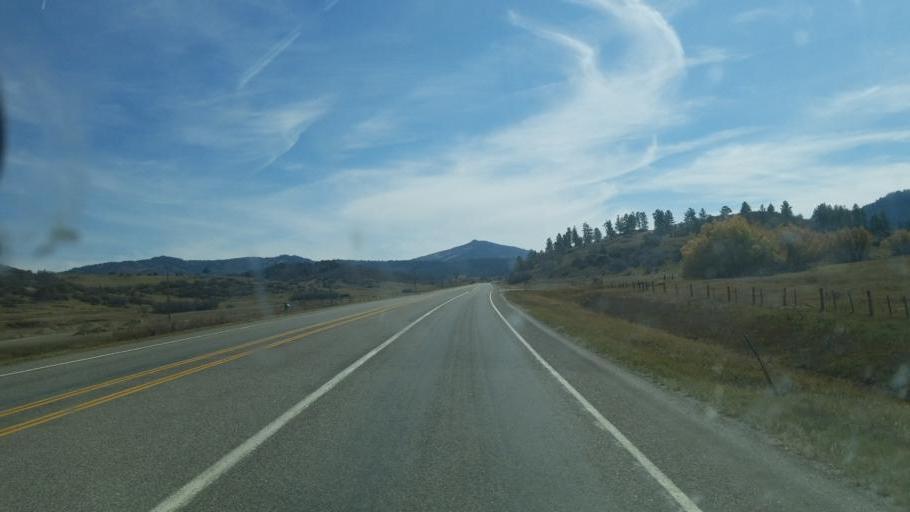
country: US
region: New Mexico
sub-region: Rio Arriba County
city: Dulce
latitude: 37.0146
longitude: -106.8066
